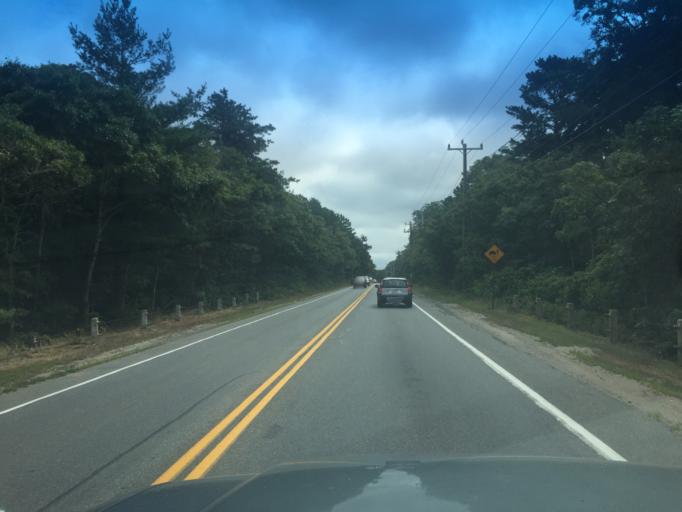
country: US
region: Massachusetts
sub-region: Barnstable County
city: East Falmouth
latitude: 41.6169
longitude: -70.5295
